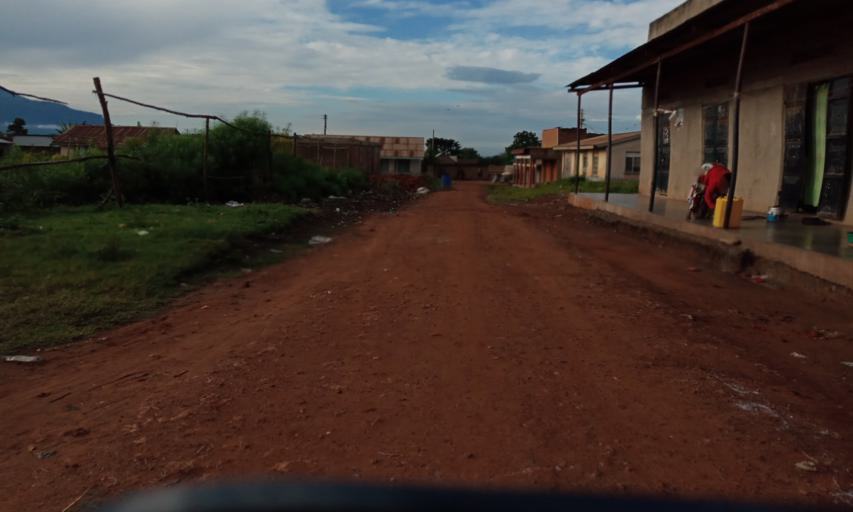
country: UG
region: Eastern Region
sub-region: Mbale District
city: Mbale
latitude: 1.1418
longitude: 34.1672
